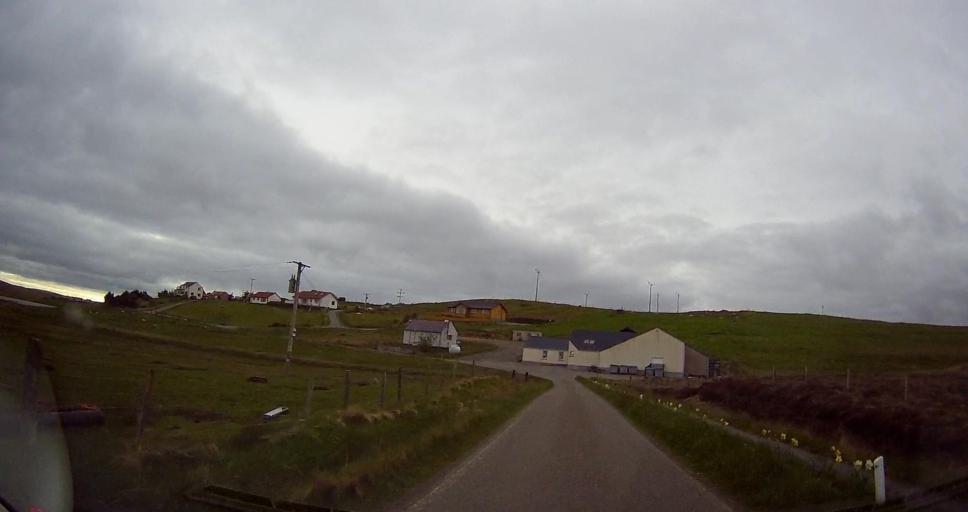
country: GB
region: Scotland
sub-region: Shetland Islands
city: Shetland
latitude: 60.5011
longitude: -1.0627
